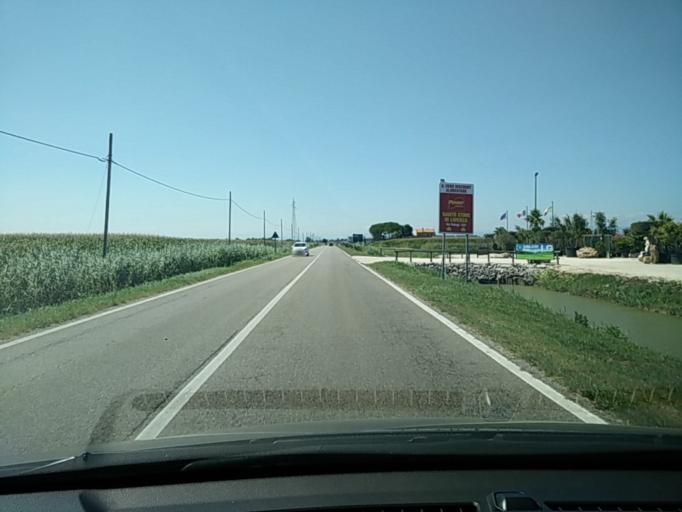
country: IT
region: Veneto
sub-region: Provincia di Venezia
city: Caorle
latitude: 45.6354
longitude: 12.8546
